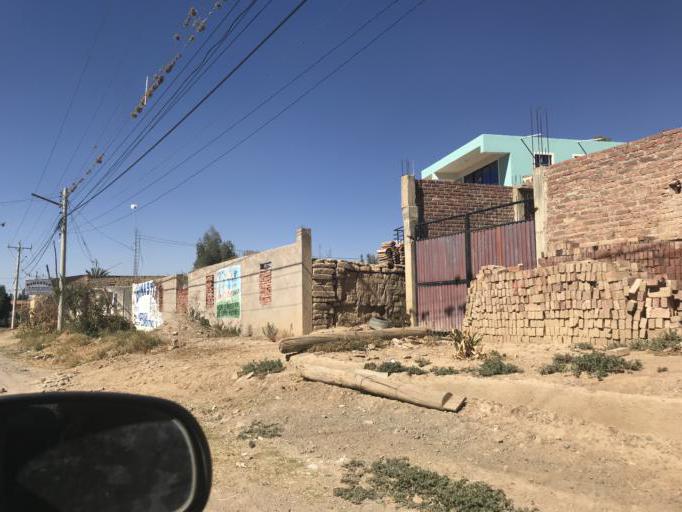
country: BO
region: Cochabamba
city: Tarata
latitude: -17.6028
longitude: -65.9845
